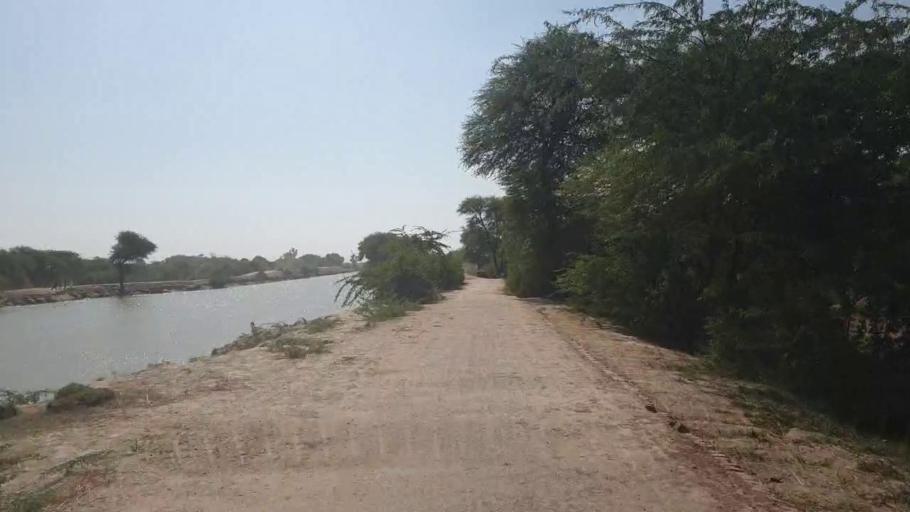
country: PK
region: Sindh
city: Talhar
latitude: 24.8250
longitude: 68.7945
